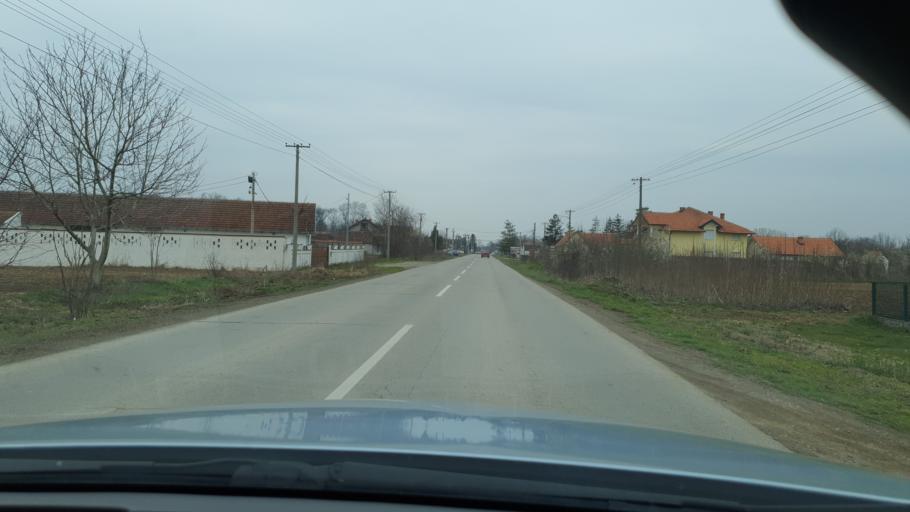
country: RS
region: Central Serbia
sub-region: Macvanski Okrug
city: Bogatic
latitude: 44.8318
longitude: 19.5036
